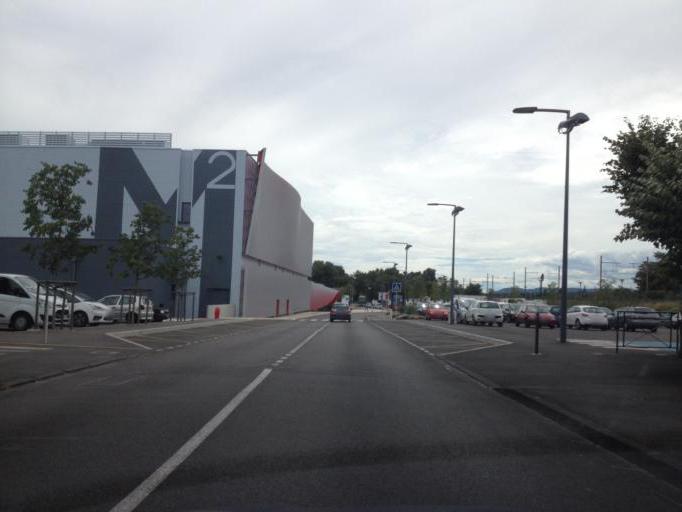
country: FR
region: Rhone-Alpes
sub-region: Departement de la Drome
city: Montelimar
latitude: 44.5563
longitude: 4.7445
